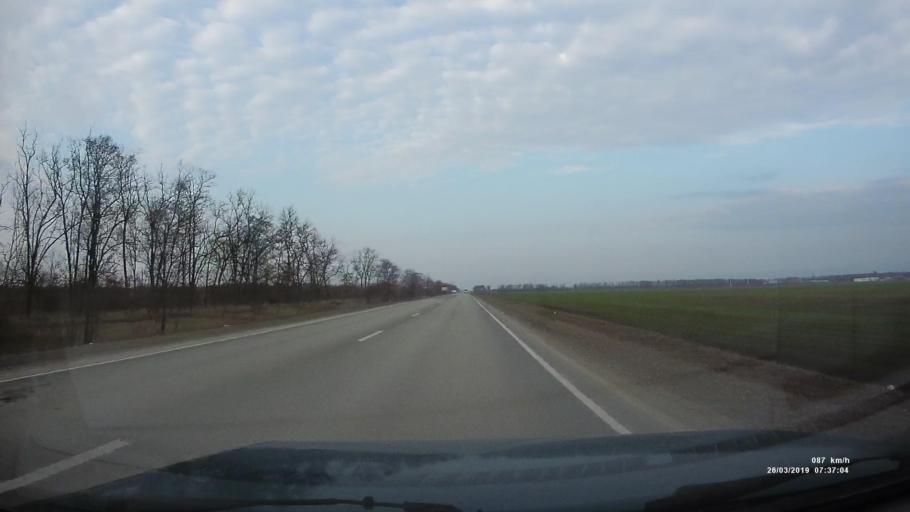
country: RU
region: Rostov
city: Novobessergenovka
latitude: 47.2034
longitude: 38.7089
